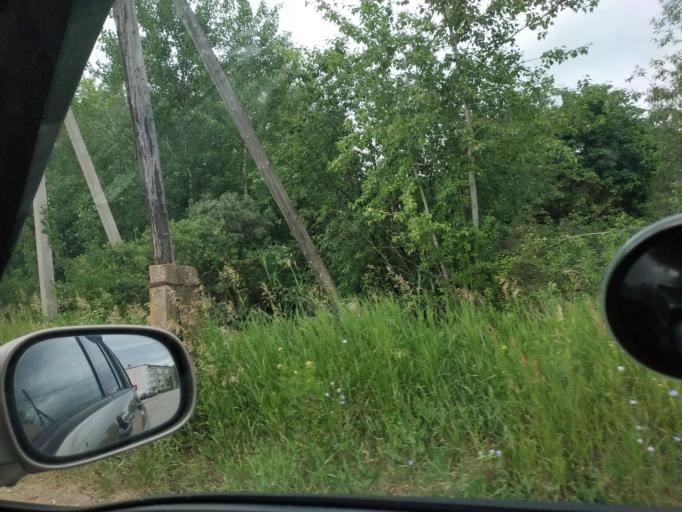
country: RU
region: Moskovskaya
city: Krasnoarmeysk
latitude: 56.0856
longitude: 38.2259
